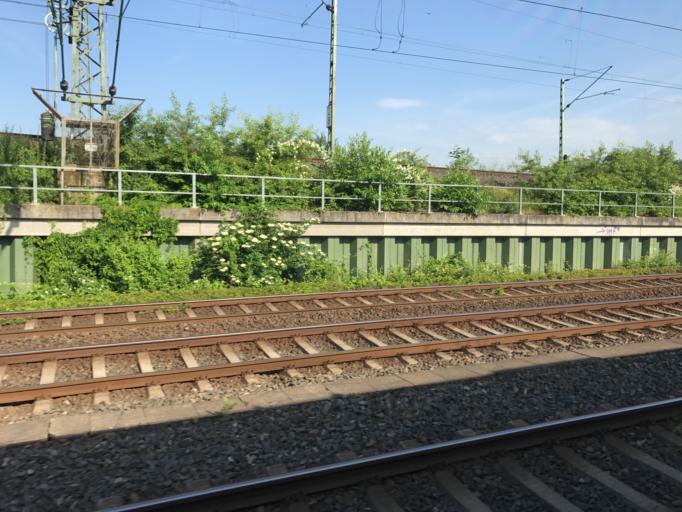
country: DE
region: Hesse
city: Niederrad
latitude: 50.0934
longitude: 8.6304
